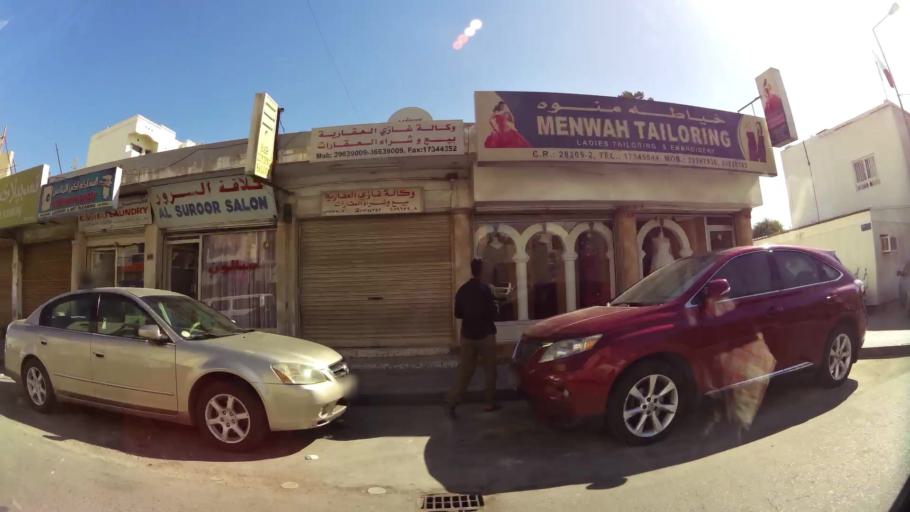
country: BH
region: Muharraq
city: Al Muharraq
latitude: 26.2553
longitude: 50.6178
